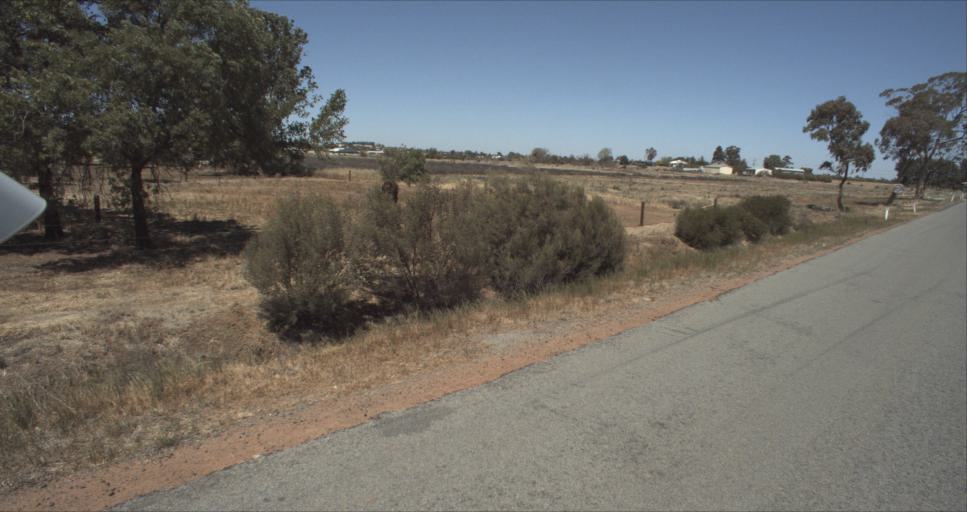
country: AU
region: New South Wales
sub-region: Leeton
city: Leeton
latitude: -34.5355
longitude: 146.3976
